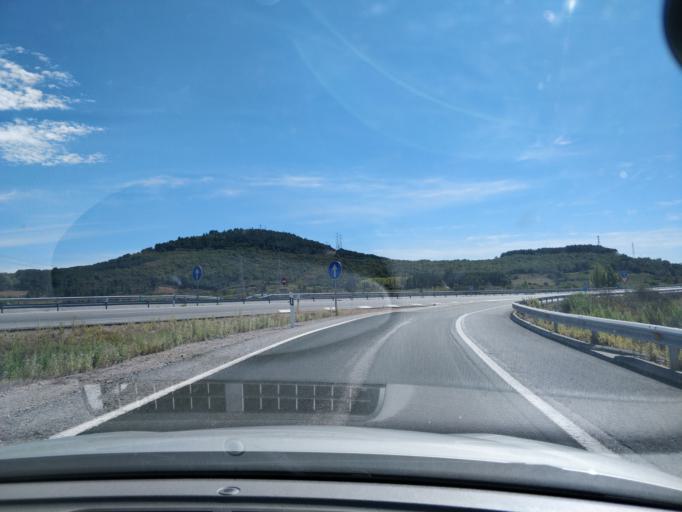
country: ES
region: Castille and Leon
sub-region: Provincia de Leon
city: Ponferrada
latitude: 42.5789
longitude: -6.6045
